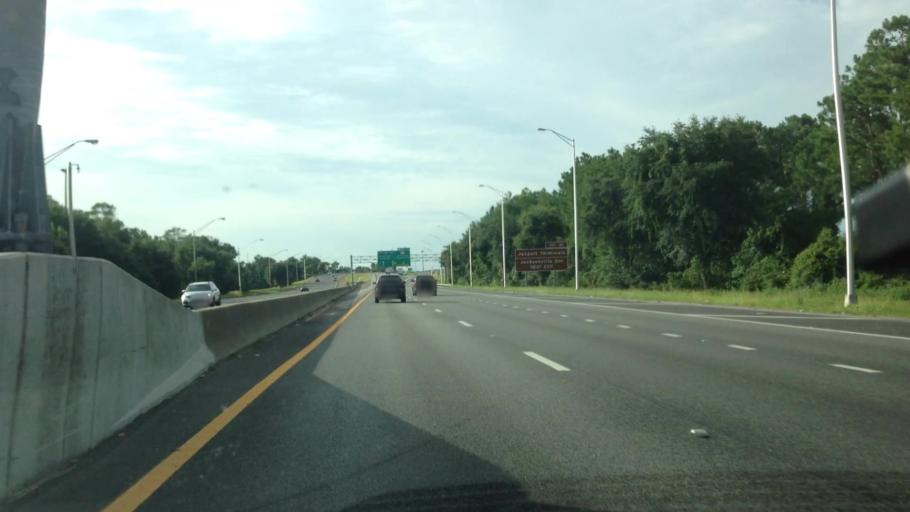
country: US
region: Florida
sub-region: Duval County
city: Jacksonville
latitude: 30.3951
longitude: -81.5634
